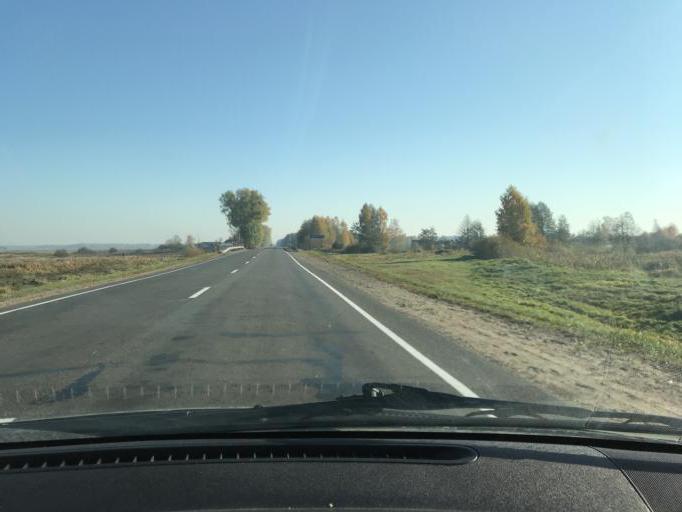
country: BY
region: Brest
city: Baranovichi
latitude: 52.8973
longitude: 25.8565
